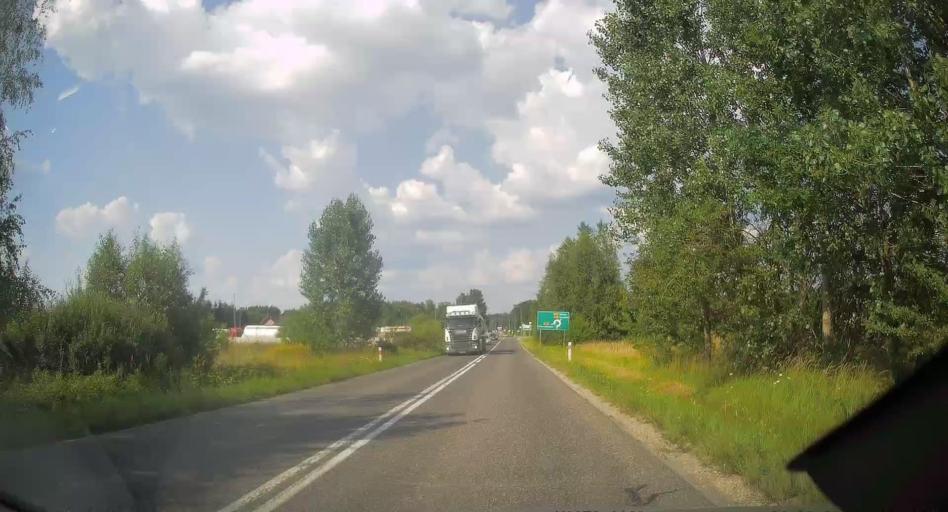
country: PL
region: Swietokrzyskie
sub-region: Powiat kielecki
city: Lopuszno
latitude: 50.9323
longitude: 20.2393
